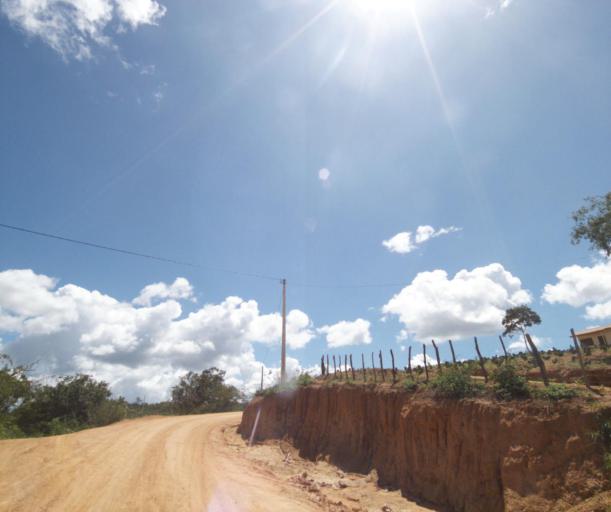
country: BR
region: Bahia
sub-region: Pocoes
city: Pocoes
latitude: -14.2991
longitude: -40.6458
